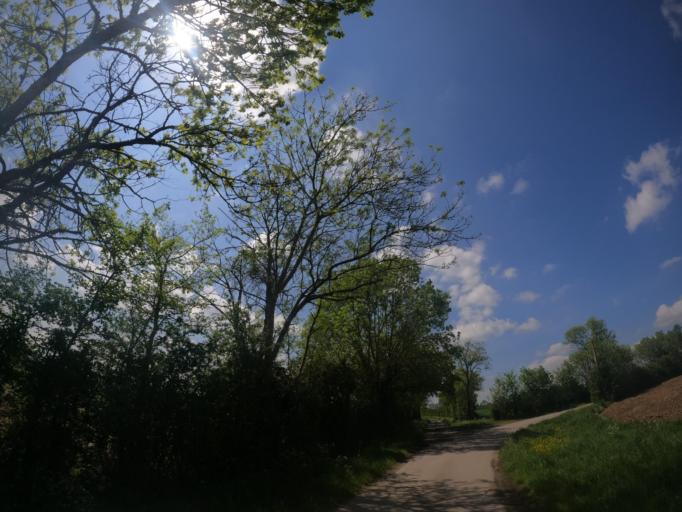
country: FR
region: Poitou-Charentes
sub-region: Departement des Deux-Sevres
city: Saint-Varent
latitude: 46.8482
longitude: -0.2798
